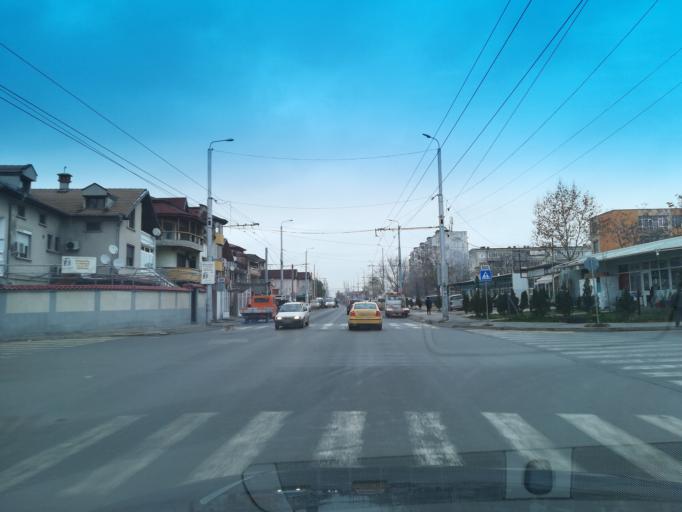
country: BG
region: Plovdiv
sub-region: Obshtina Plovdiv
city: Plovdiv
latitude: 42.1562
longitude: 24.7880
